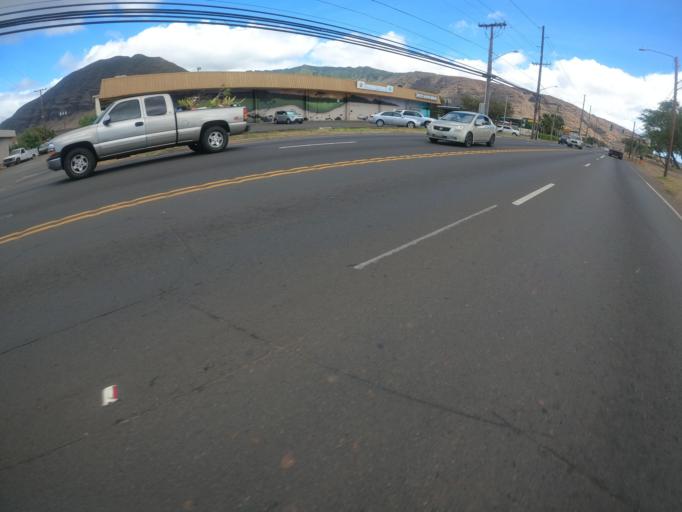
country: US
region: Hawaii
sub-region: Honolulu County
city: Nanakuli
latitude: 21.3863
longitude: -158.1507
